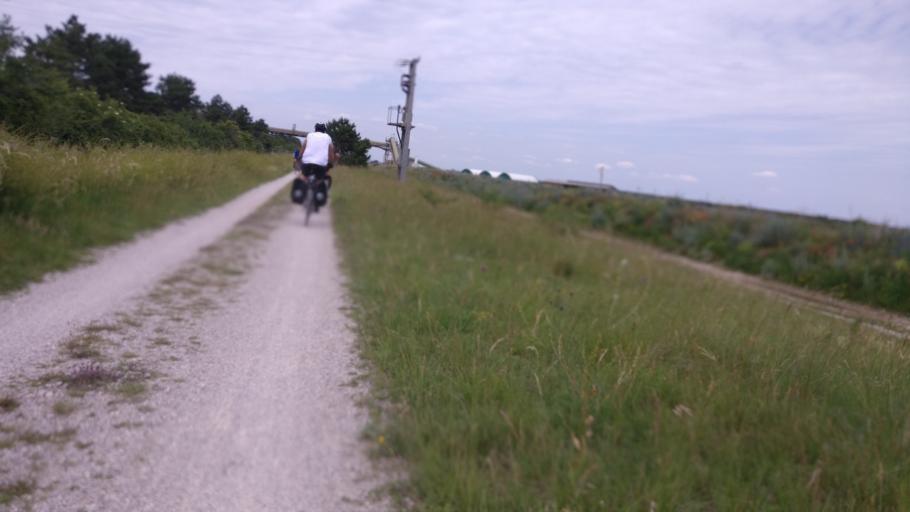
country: AT
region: Lower Austria
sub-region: Politischer Bezirk Wiener Neustadt
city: Sollenau
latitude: 47.8741
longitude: 16.2813
